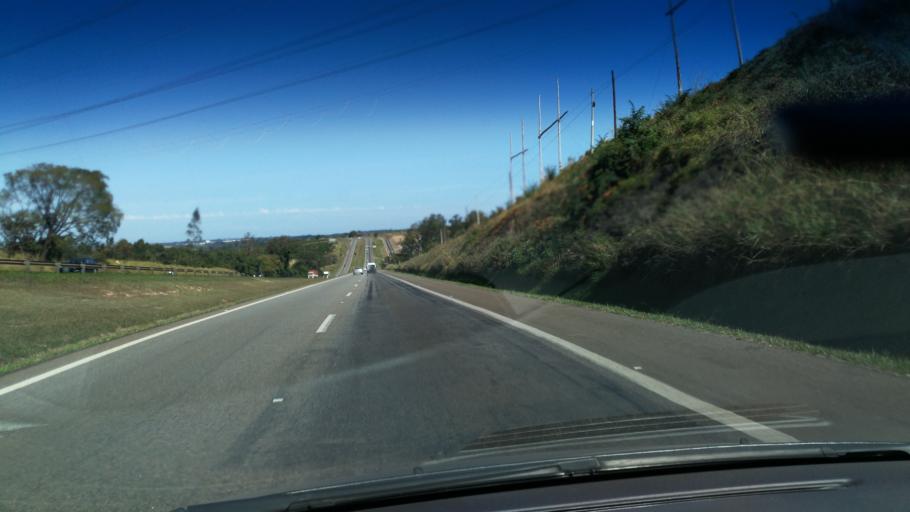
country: BR
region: Sao Paulo
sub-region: Santo Antonio De Posse
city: Santo Antonio de Posse
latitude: -22.5347
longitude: -46.9952
